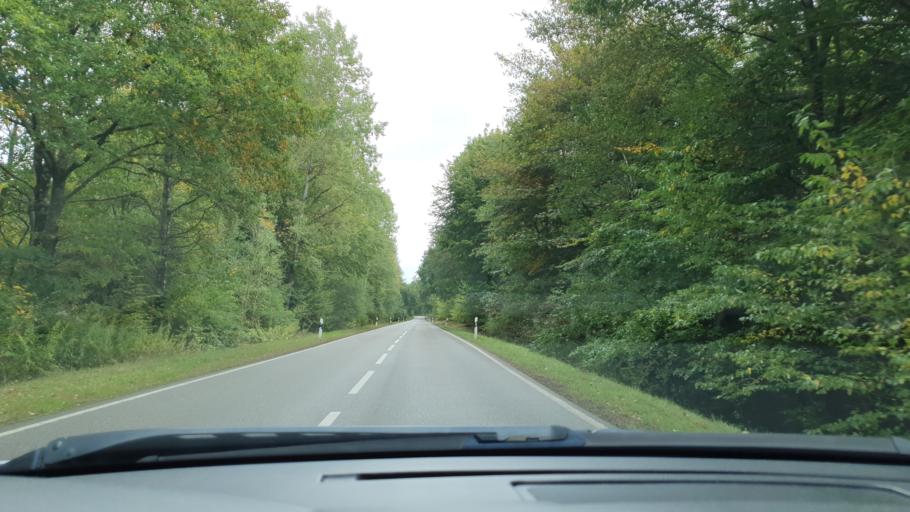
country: DE
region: Rheinland-Pfalz
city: Kaiserslautern
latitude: 49.4360
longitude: 7.8125
